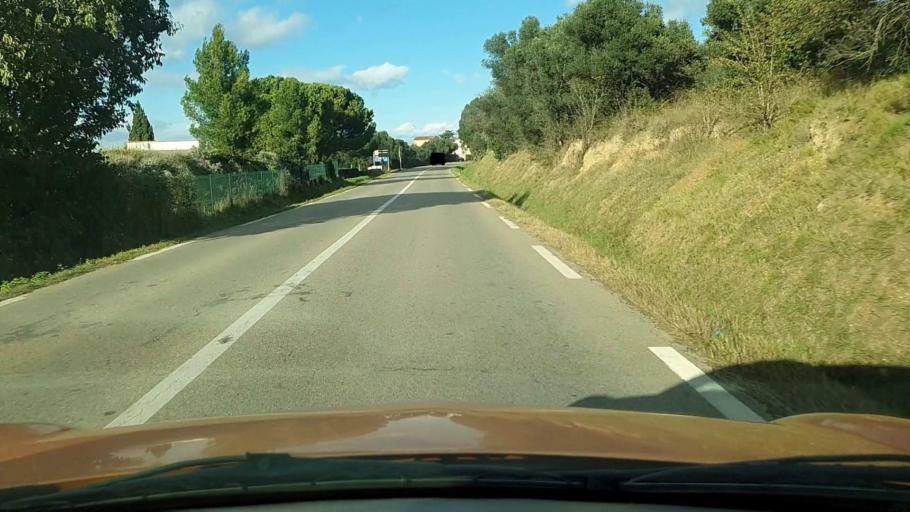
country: FR
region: Languedoc-Roussillon
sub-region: Departement du Gard
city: Vauvert
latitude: 43.6852
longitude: 4.2738
